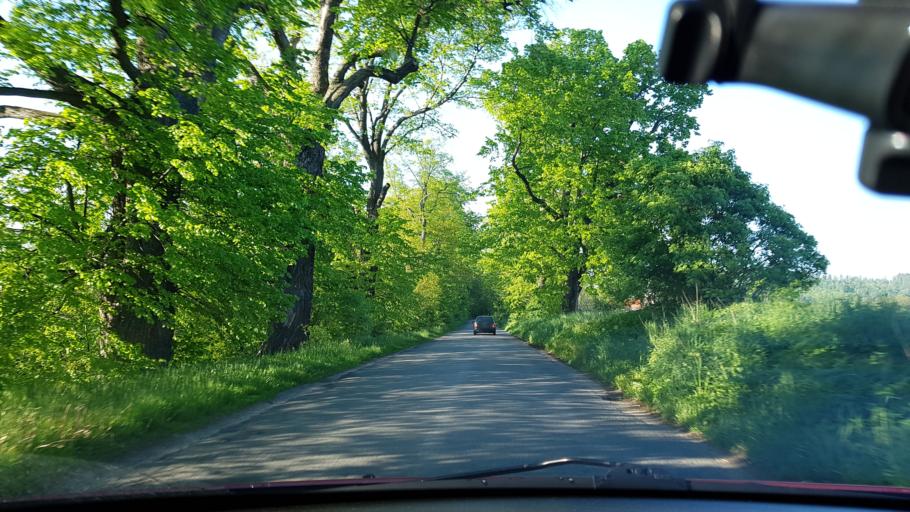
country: PL
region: Lower Silesian Voivodeship
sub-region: Powiat zabkowicki
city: Budzow
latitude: 50.6069
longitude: 16.6703
